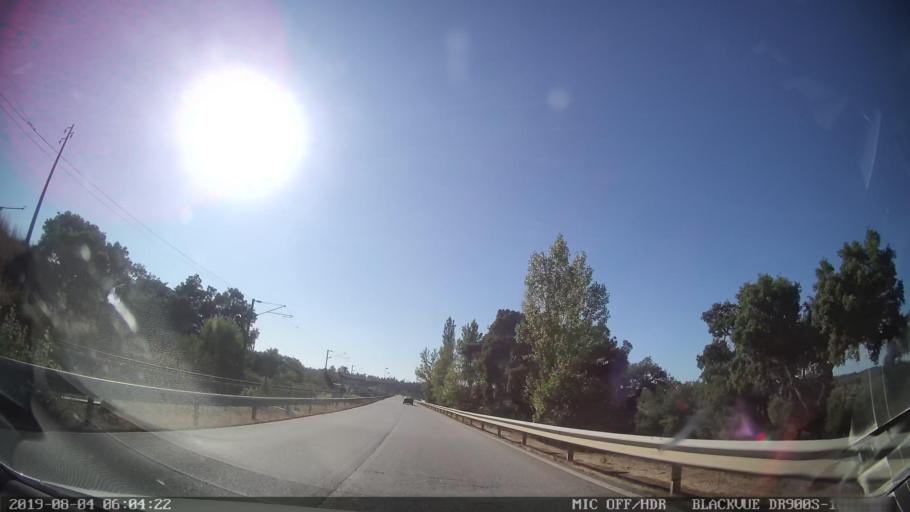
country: PT
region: Santarem
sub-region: Abrantes
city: Alferrarede
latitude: 39.4694
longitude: -8.0617
